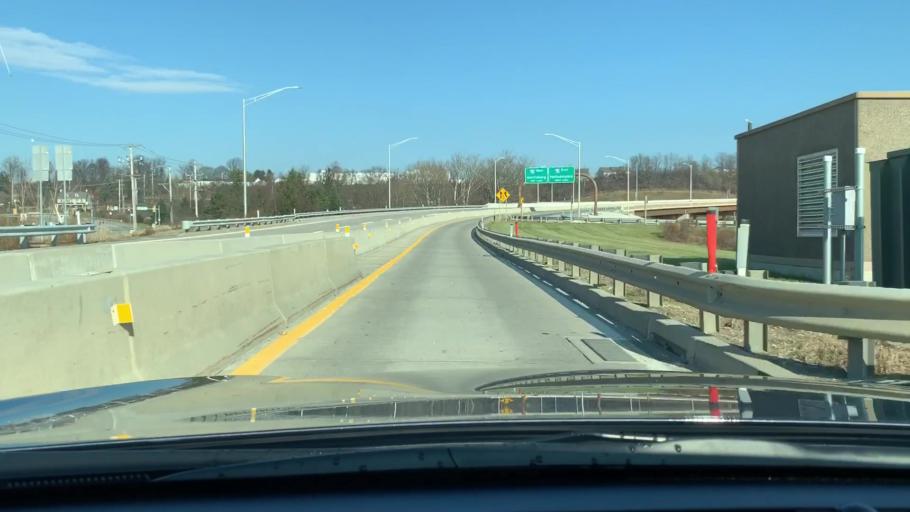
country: US
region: Pennsylvania
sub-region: Chester County
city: Malvern
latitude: 40.0716
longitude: -75.5351
